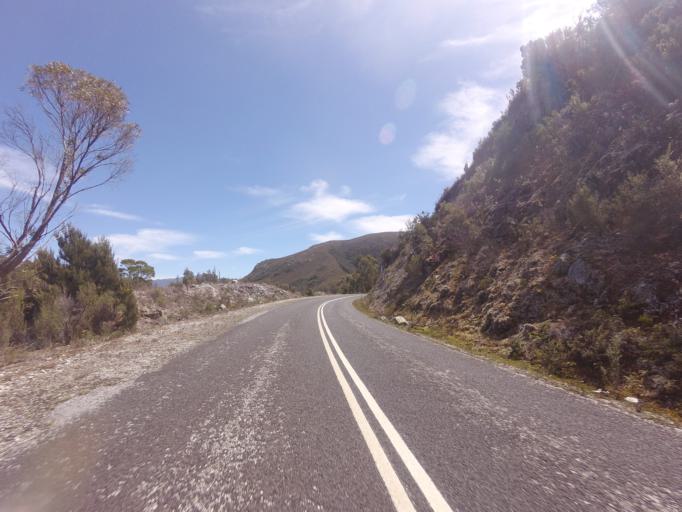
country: AU
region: Tasmania
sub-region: West Coast
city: Queenstown
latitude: -42.7981
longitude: 146.0889
